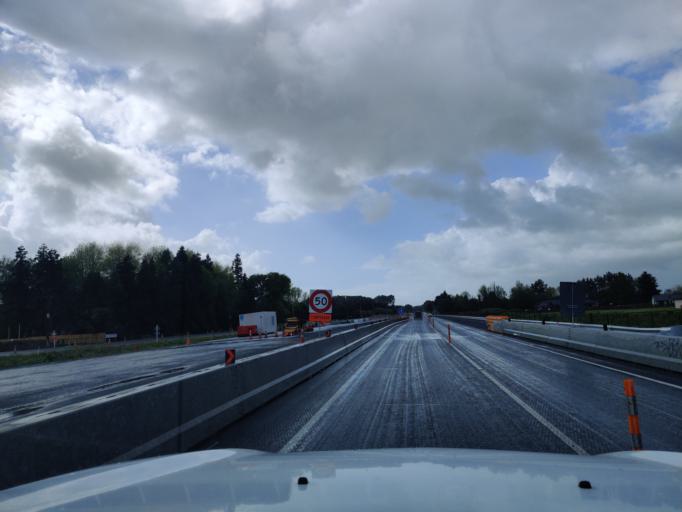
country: NZ
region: Waikato
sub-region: Hamilton City
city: Hamilton
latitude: -37.8208
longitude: 175.3474
